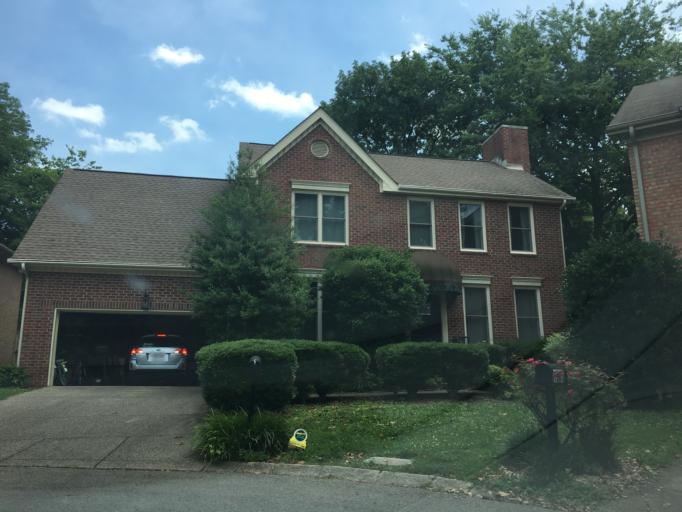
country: US
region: Tennessee
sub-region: Davidson County
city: Oak Hill
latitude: 36.0994
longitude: -86.8106
